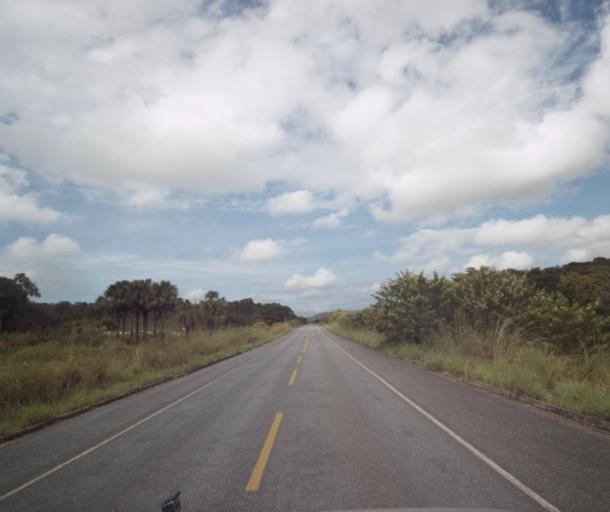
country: BR
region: Goias
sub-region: Pirenopolis
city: Pirenopolis
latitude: -15.6154
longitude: -48.6600
